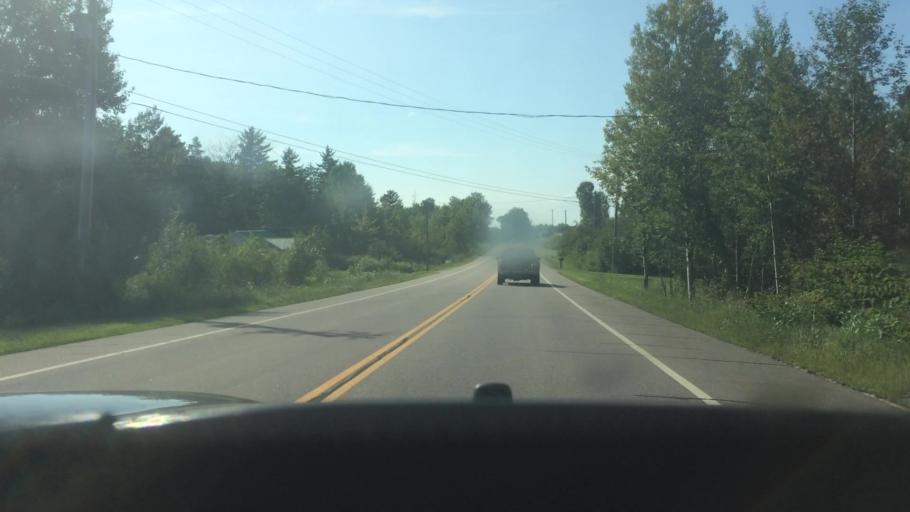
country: US
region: New York
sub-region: Franklin County
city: Malone
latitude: 44.8559
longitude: -74.2250
